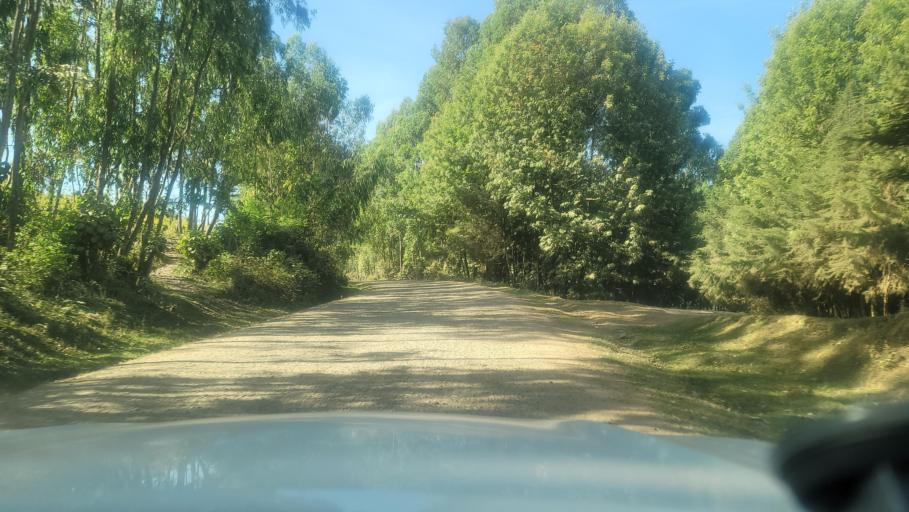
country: ET
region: Oromiya
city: Agaro
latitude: 7.8048
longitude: 36.5007
